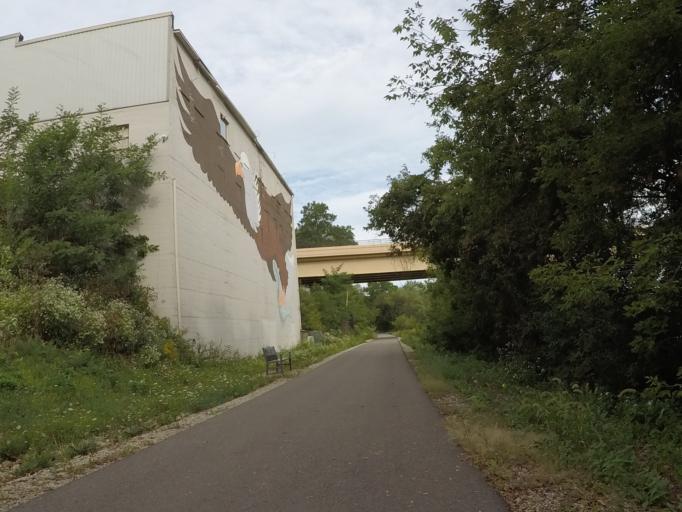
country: US
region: Wisconsin
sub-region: Sauk County
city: Prairie du Sac
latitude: 43.2927
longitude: -89.7219
